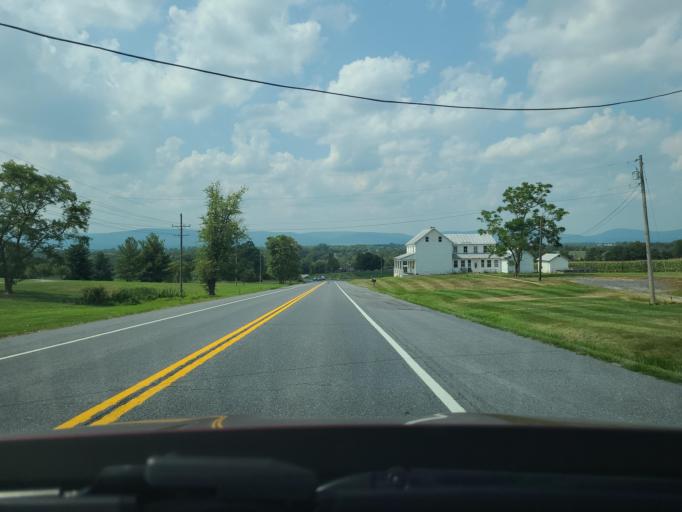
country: US
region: Maryland
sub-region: Frederick County
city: Woodsboro
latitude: 39.5591
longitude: -77.3456
